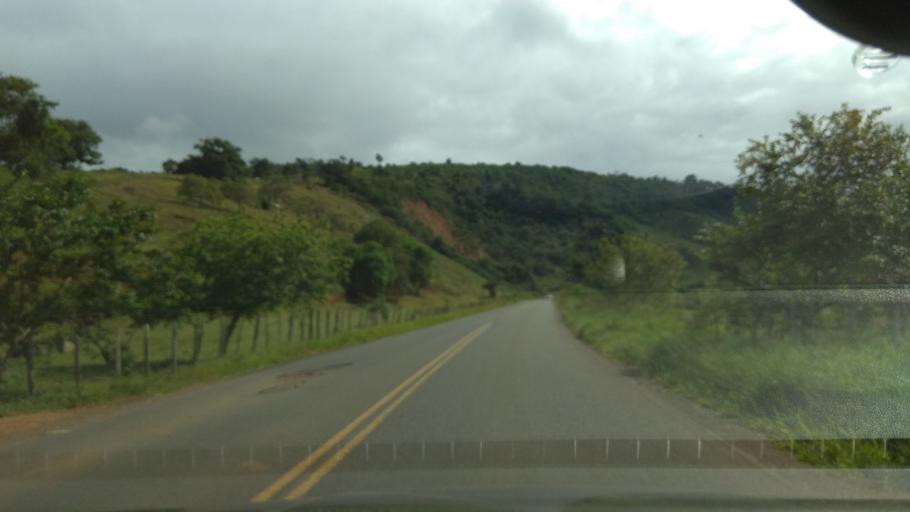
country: BR
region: Bahia
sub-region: Ubaira
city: Ubaira
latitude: -13.2585
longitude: -39.6773
